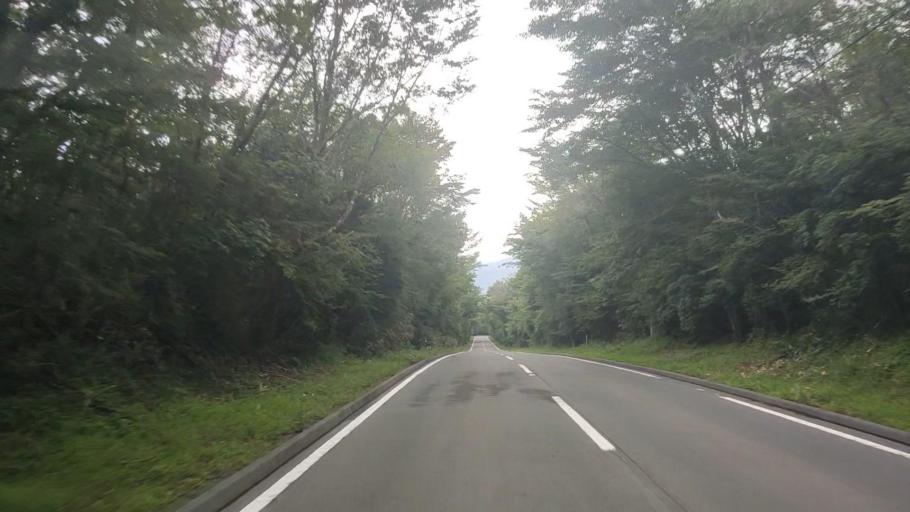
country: JP
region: Shizuoka
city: Gotemba
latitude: 35.2749
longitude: 138.7964
